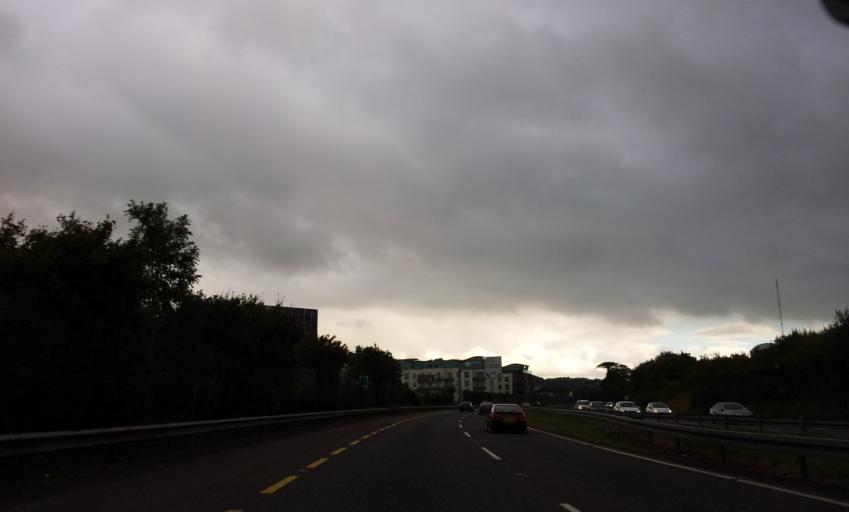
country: IE
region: Munster
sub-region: County Cork
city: Passage West
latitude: 51.8880
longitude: -8.3908
